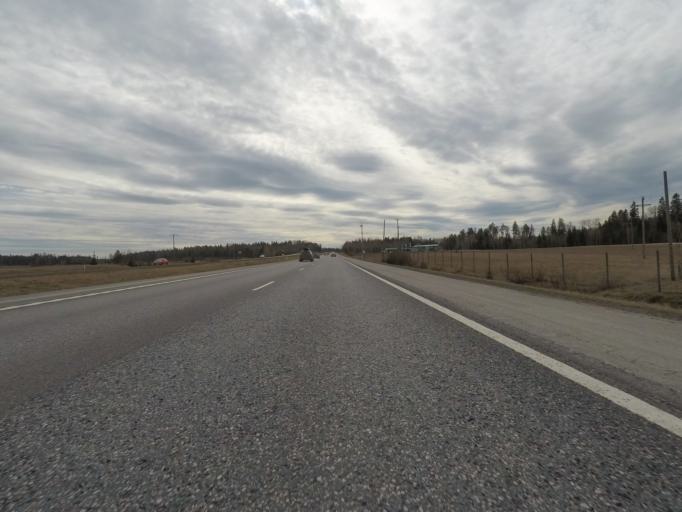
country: FI
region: Paijanne Tavastia
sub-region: Lahti
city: Lahti
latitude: 60.9084
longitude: 25.6138
